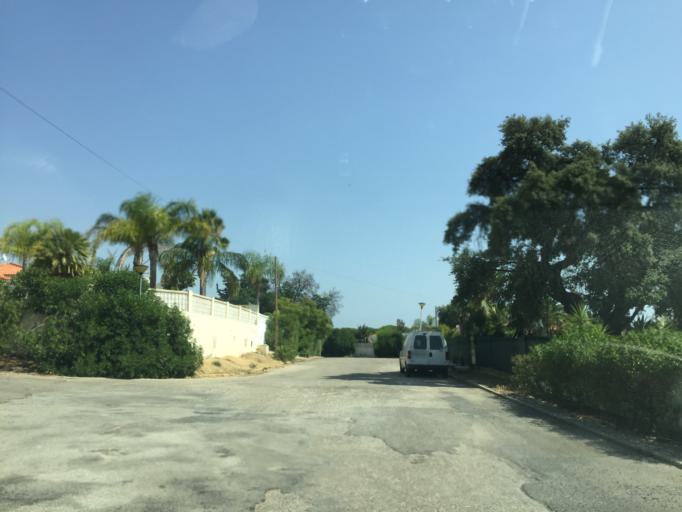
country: PT
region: Faro
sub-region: Albufeira
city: Ferreiras
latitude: 37.1053
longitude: -8.2034
